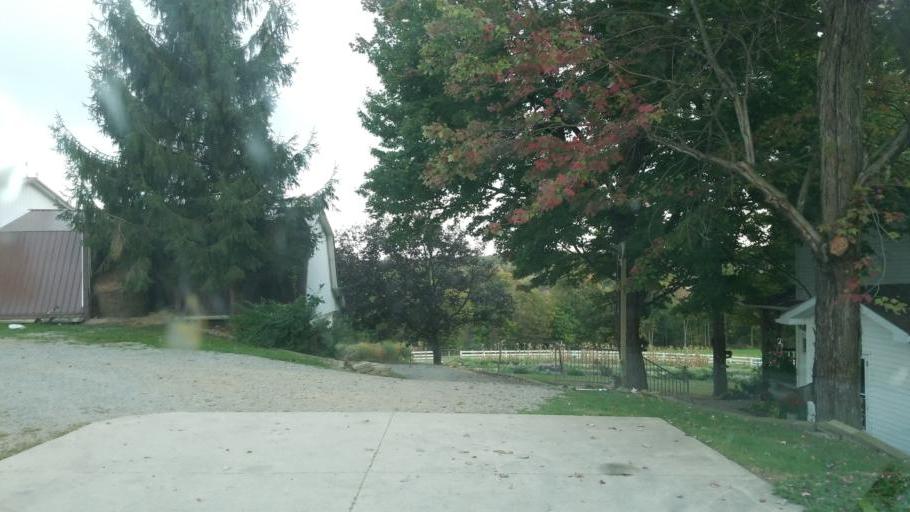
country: US
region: Ohio
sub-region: Knox County
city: Danville
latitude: 40.5310
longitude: -82.3597
